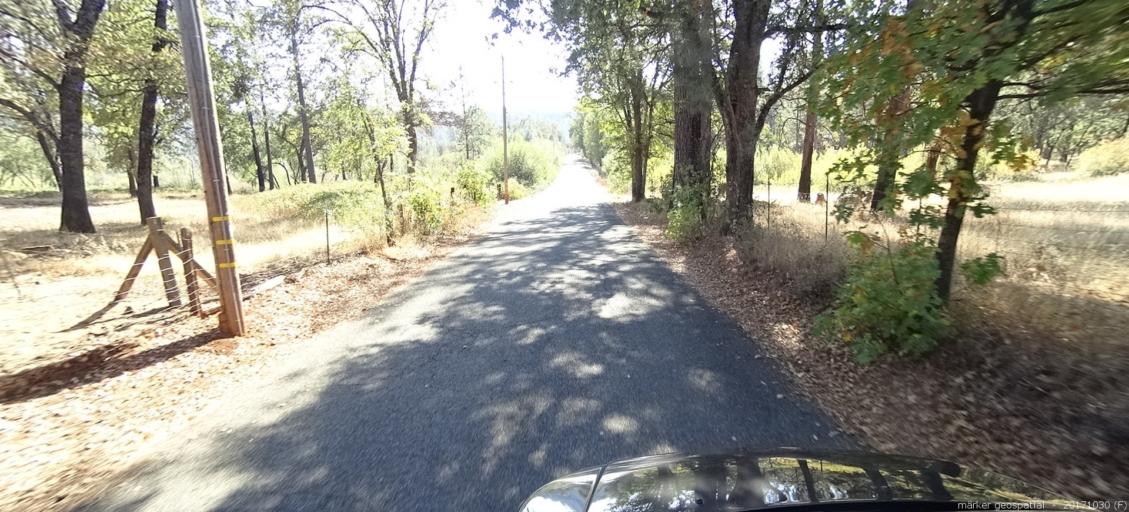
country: US
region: California
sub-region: Shasta County
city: Shingletown
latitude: 40.5229
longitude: -121.9644
